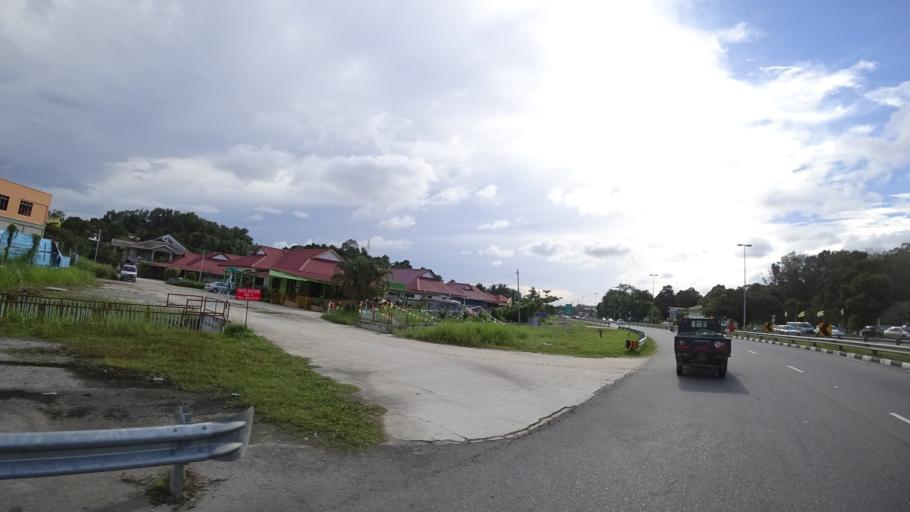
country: BN
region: Brunei and Muara
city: Bandar Seri Begawan
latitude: 4.8805
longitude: 114.8758
